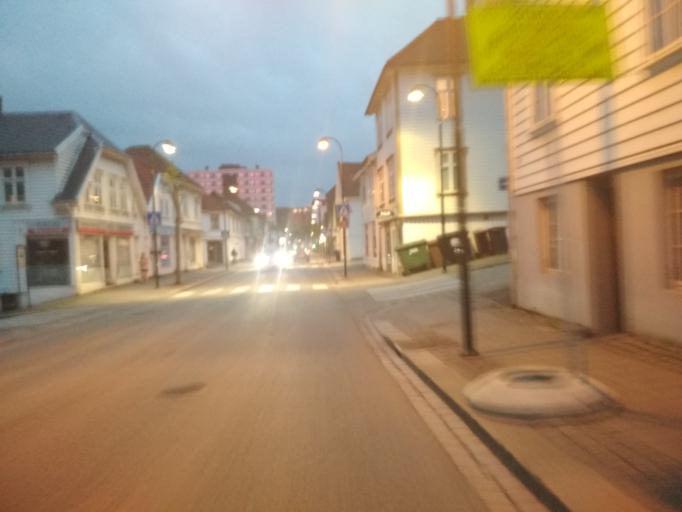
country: NO
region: Rogaland
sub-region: Stavanger
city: Stavanger
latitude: 58.9712
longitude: 5.7241
